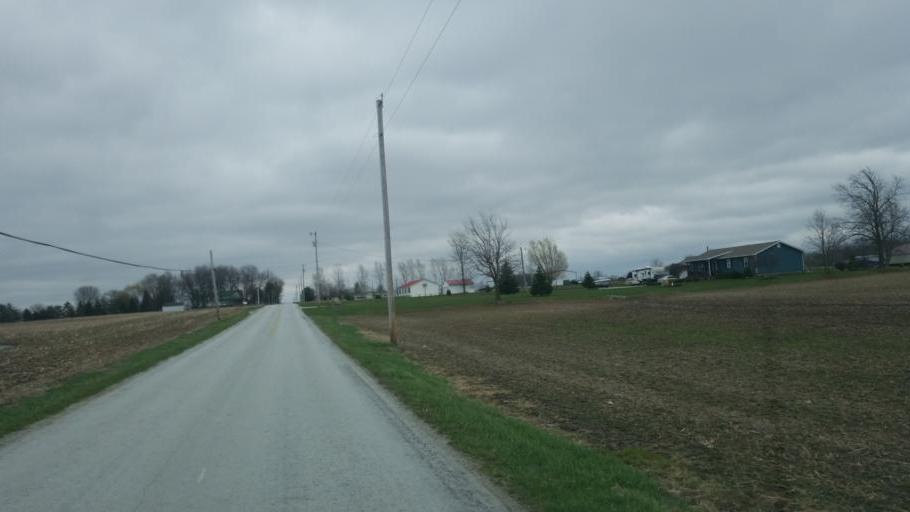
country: US
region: Ohio
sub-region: Hardin County
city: Kenton
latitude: 40.6585
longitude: -83.5532
